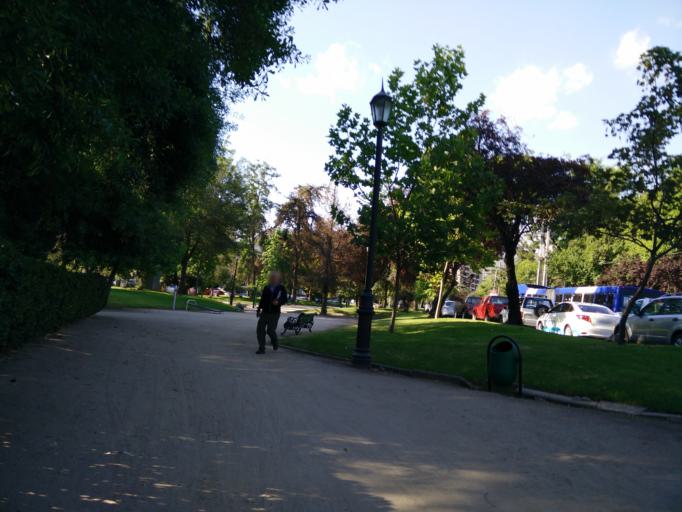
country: CL
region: Santiago Metropolitan
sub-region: Provincia de Santiago
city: Villa Presidente Frei, Nunoa, Santiago, Chile
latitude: -33.4088
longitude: -70.5872
